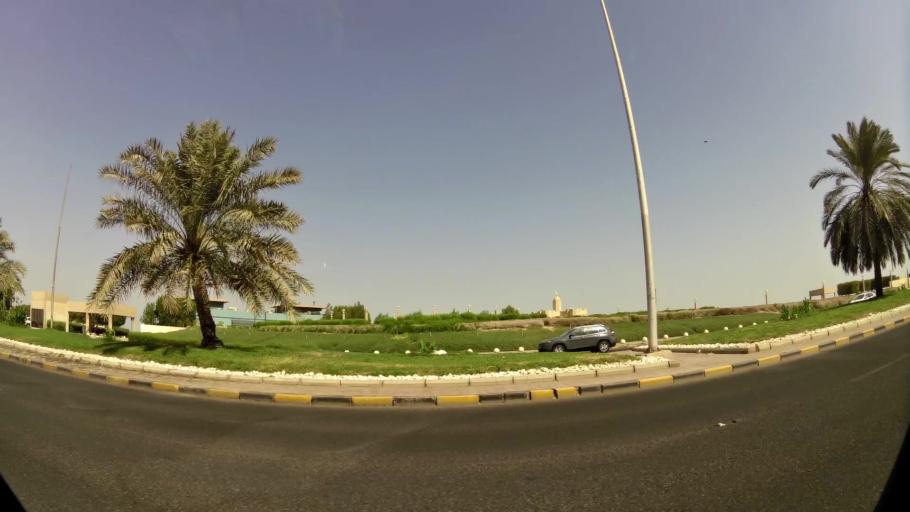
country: KW
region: Muhafazat Hawalli
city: Hawalli
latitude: 29.3509
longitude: 48.0321
